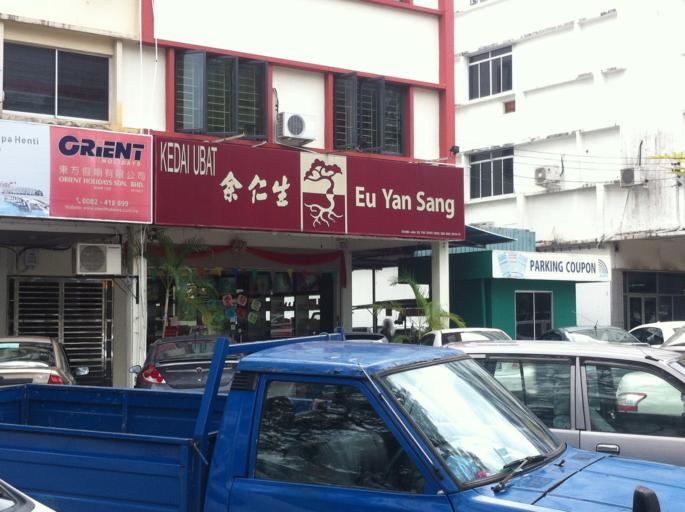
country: MY
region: Sarawak
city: Kuching
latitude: 1.5555
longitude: 110.3536
